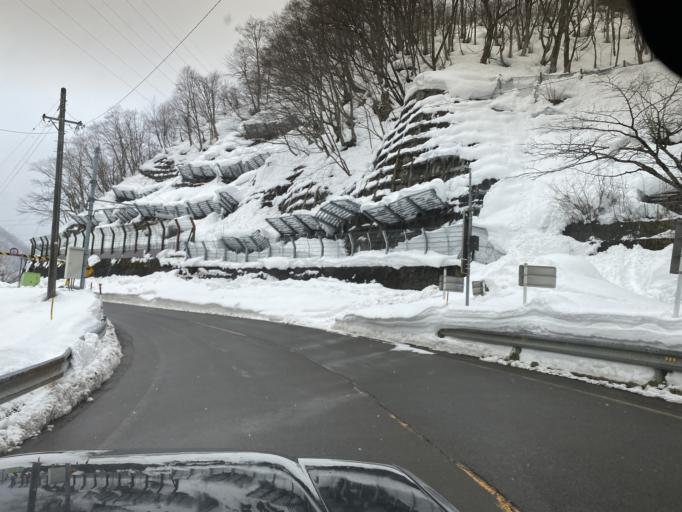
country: JP
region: Gifu
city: Takayama
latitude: 36.1434
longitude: 136.9058
